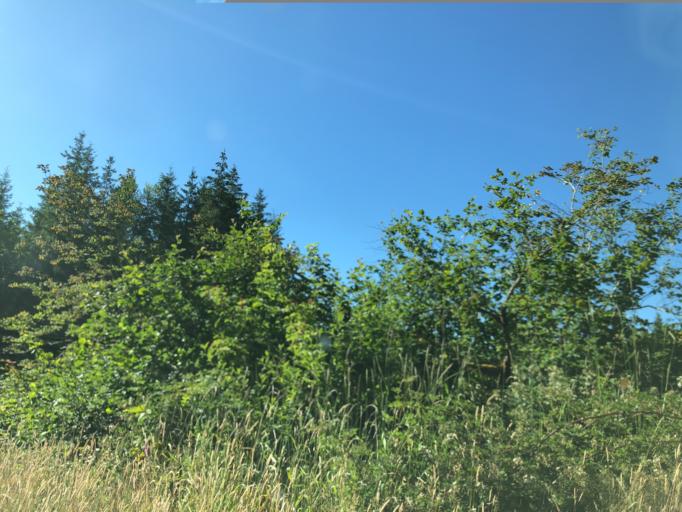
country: US
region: Oregon
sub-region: Linn County
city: Sweet Home
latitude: 44.4646
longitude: -122.6708
